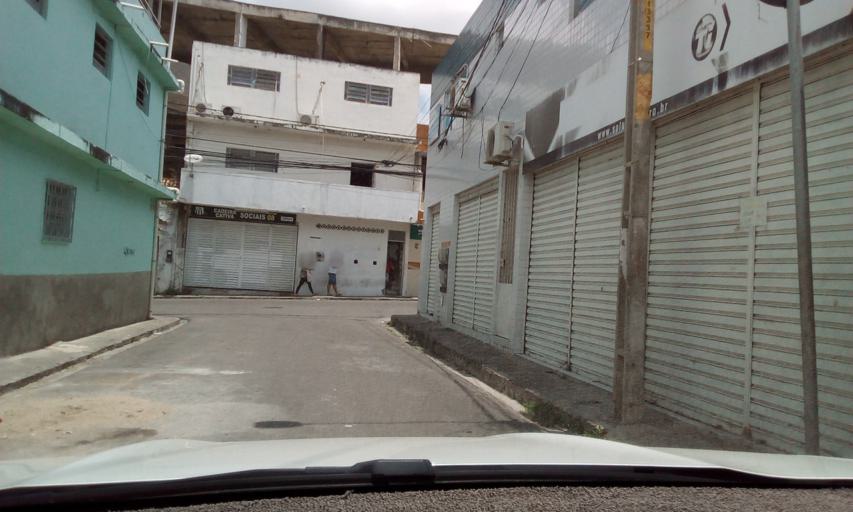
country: BR
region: Pernambuco
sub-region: Caruaru
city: Caruaru
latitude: -8.2778
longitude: -35.9737
